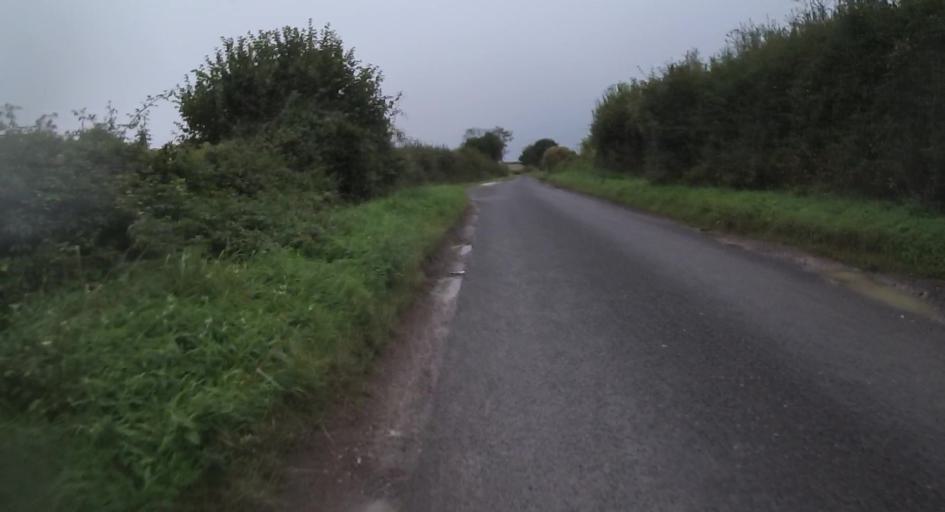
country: GB
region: England
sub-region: Hampshire
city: Basingstoke
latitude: 51.2945
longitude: -1.1301
